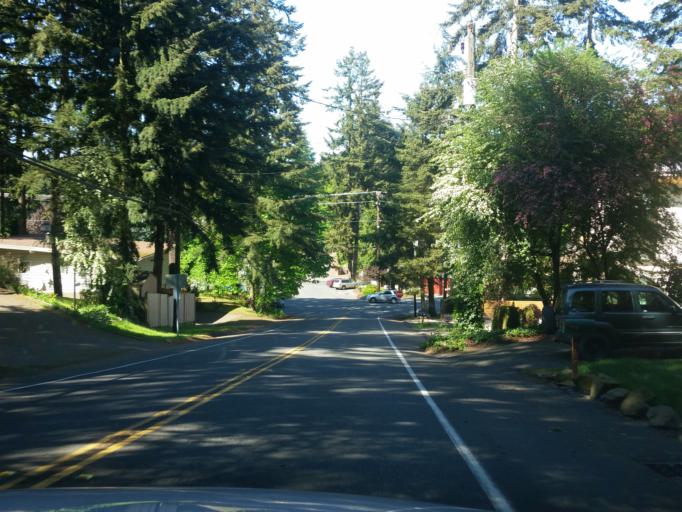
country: US
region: Washington
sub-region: Snohomish County
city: Esperance
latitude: 47.7769
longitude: -122.3612
